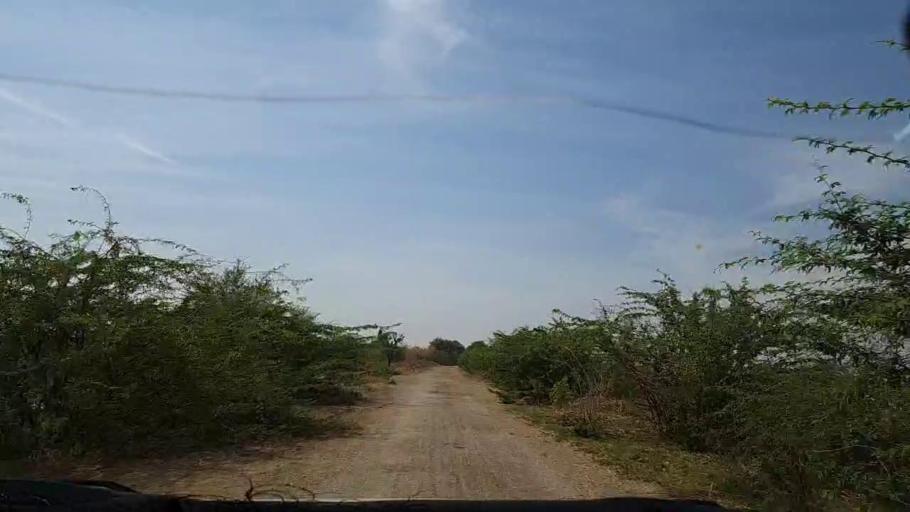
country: PK
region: Sindh
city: Pithoro
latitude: 25.4828
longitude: 69.4433
